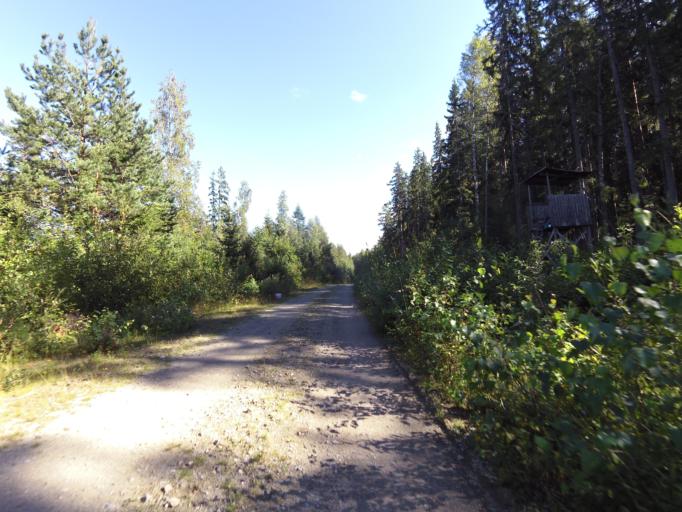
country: SE
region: Gaevleborg
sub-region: Hofors Kommun
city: Hofors
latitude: 60.5462
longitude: 16.4334
